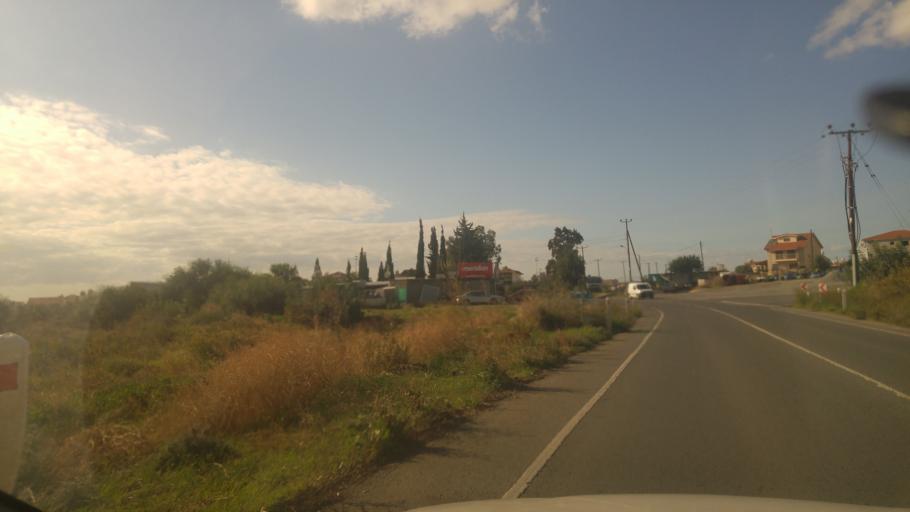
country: CY
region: Larnaka
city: Kolossi
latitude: 34.6766
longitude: 32.9440
